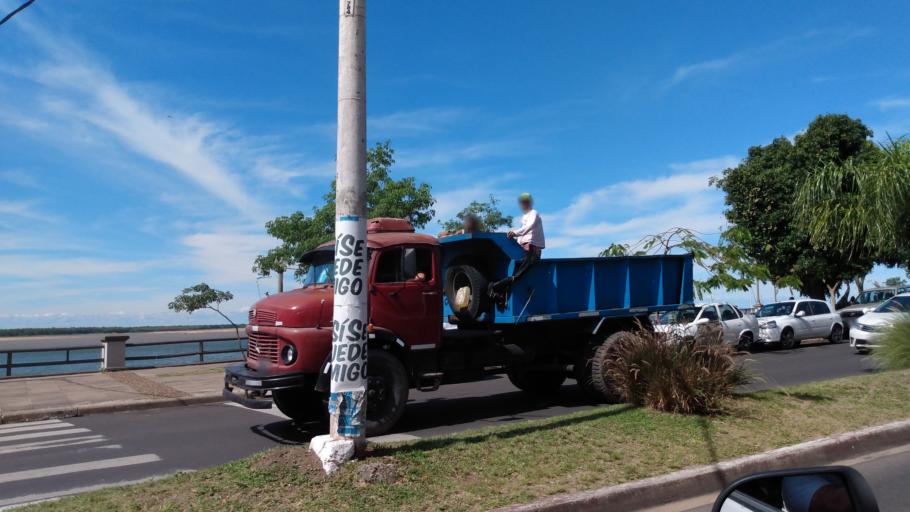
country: AR
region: Corrientes
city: Corrientes
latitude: -27.4616
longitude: -58.8400
